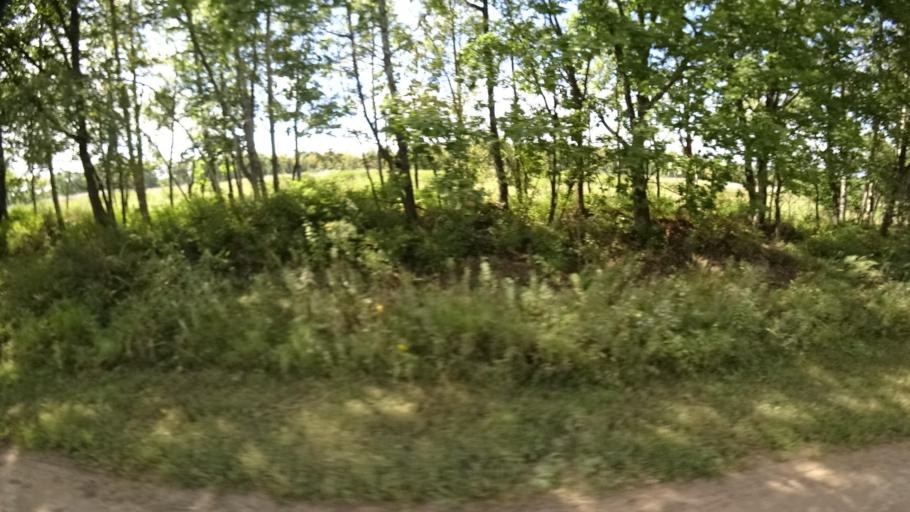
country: RU
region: Primorskiy
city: Yakovlevka
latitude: 44.4203
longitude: 133.5712
